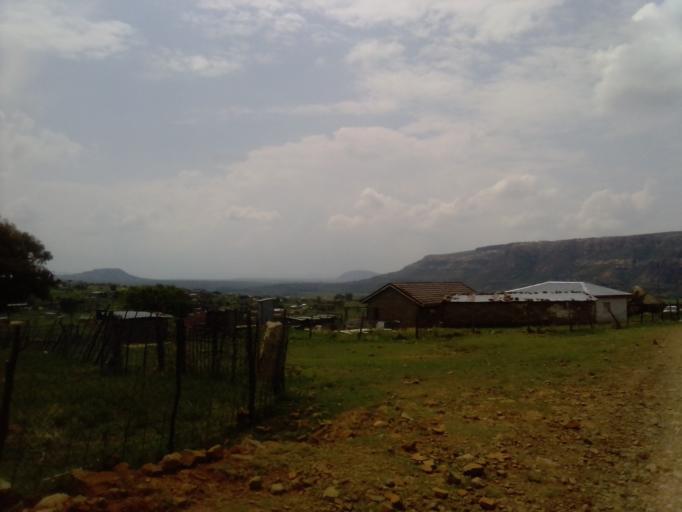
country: LS
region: Leribe
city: Leribe
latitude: -29.0247
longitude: 28.0165
